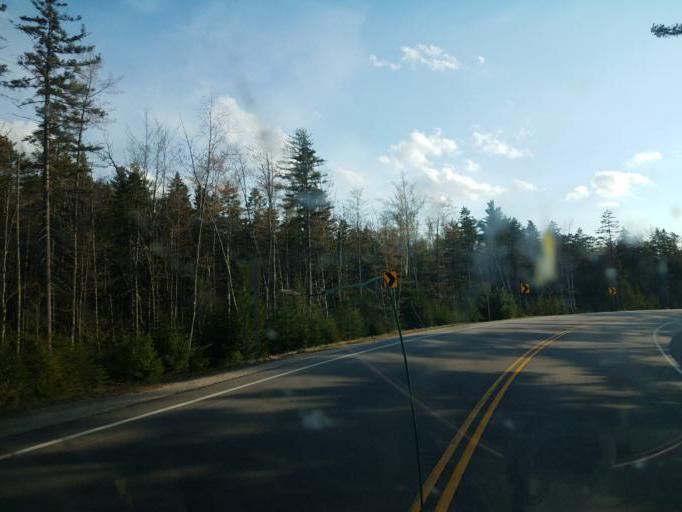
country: US
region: New Hampshire
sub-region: Carroll County
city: Tamworth
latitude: 43.9962
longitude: -71.2806
